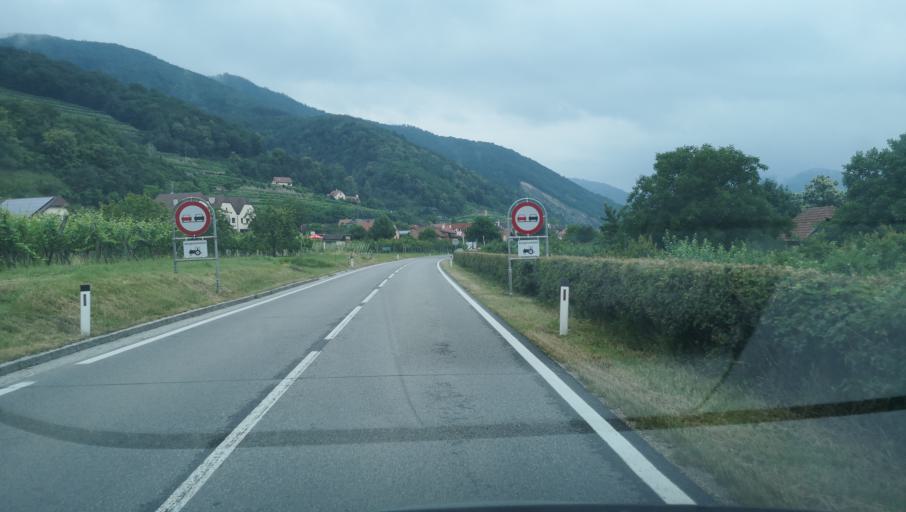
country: AT
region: Lower Austria
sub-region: Politischer Bezirk Krems
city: Spitz
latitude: 48.3351
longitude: 15.4043
